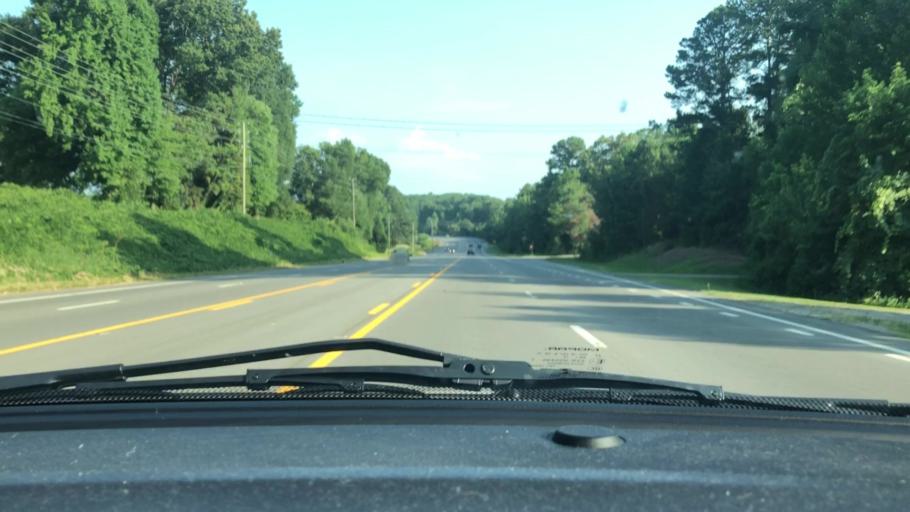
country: US
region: North Carolina
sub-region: Lee County
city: Broadway
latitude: 35.4059
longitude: -79.1150
